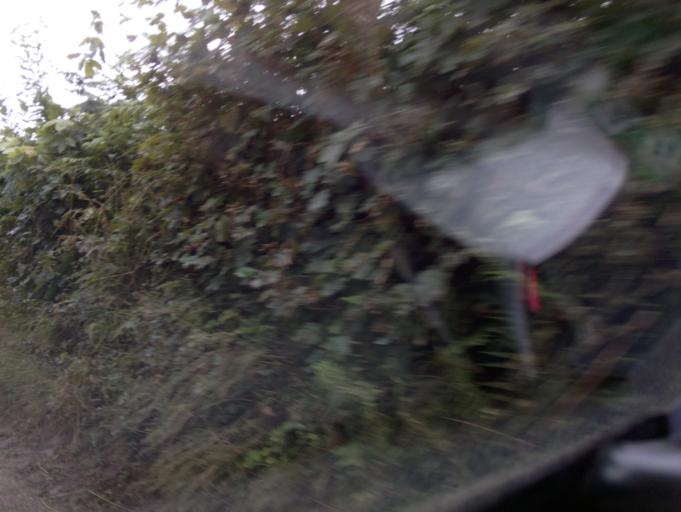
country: GB
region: England
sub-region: Devon
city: Totnes
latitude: 50.3517
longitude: -3.6667
